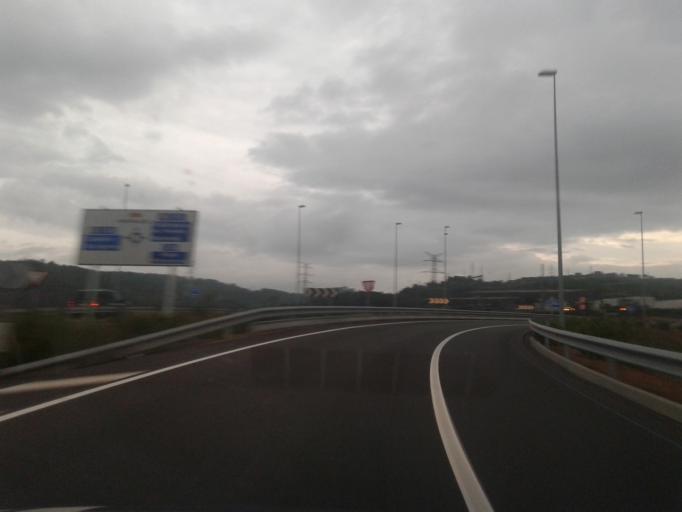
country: ES
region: Catalonia
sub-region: Provincia de Barcelona
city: Vilanova i la Geltru
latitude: 41.2519
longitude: 1.7189
